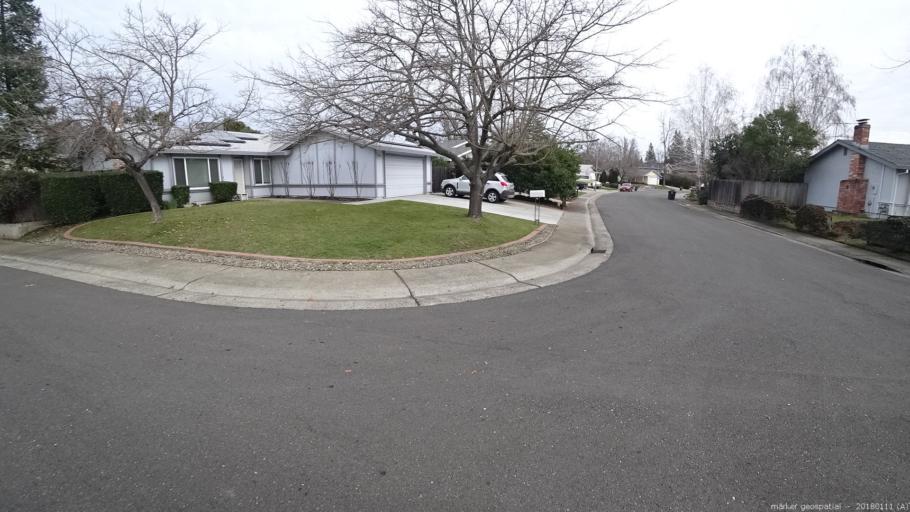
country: US
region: California
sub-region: Sacramento County
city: Fair Oaks
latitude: 38.6190
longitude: -121.2770
